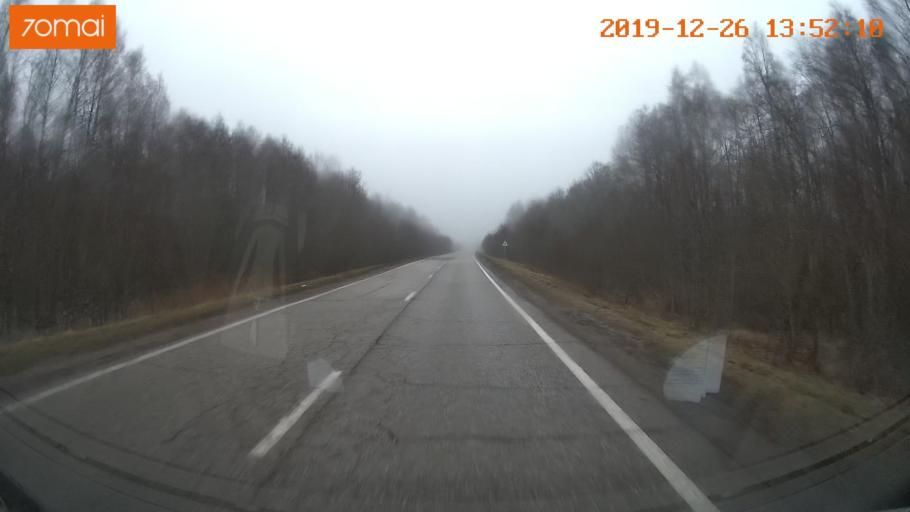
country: RU
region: Jaroslavl
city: Poshekhon'ye
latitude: 58.6354
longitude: 38.5992
